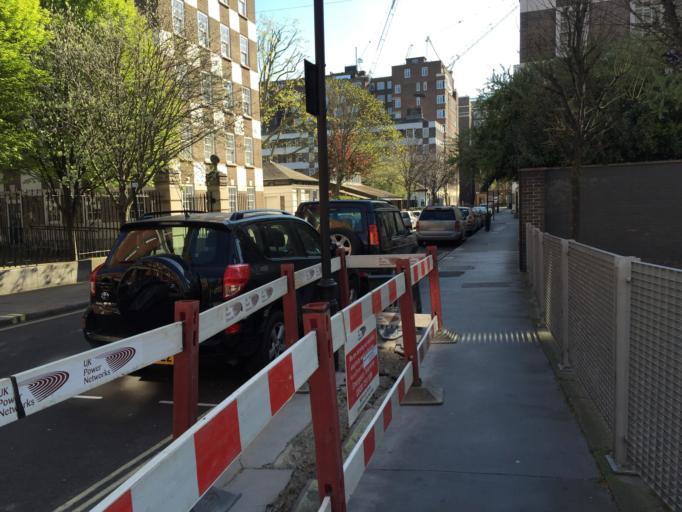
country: GB
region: England
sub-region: Greater London
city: City of Westminster
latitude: 51.4929
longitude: -0.1311
